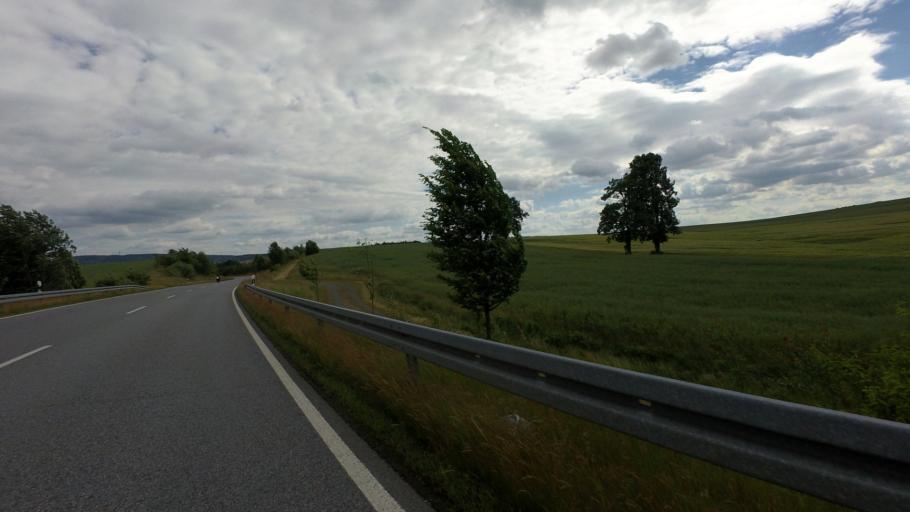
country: DE
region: Saxony
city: Berthelsdorf
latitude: 51.0423
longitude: 14.2137
